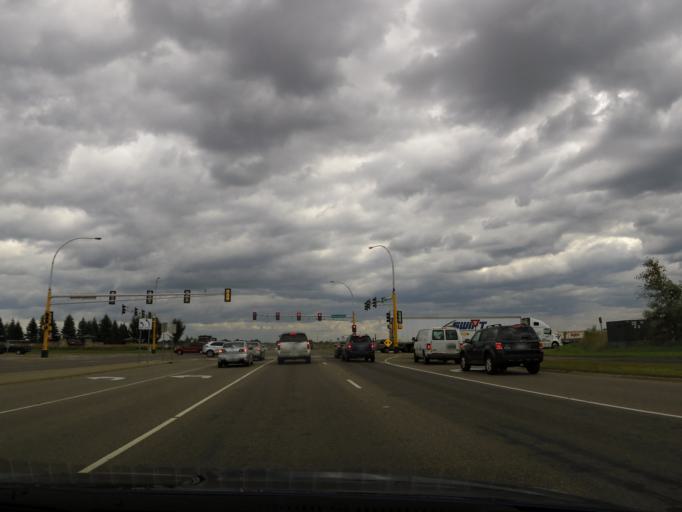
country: US
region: Minnesota
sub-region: Dakota County
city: Apple Valley
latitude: 44.7173
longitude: -93.1777
